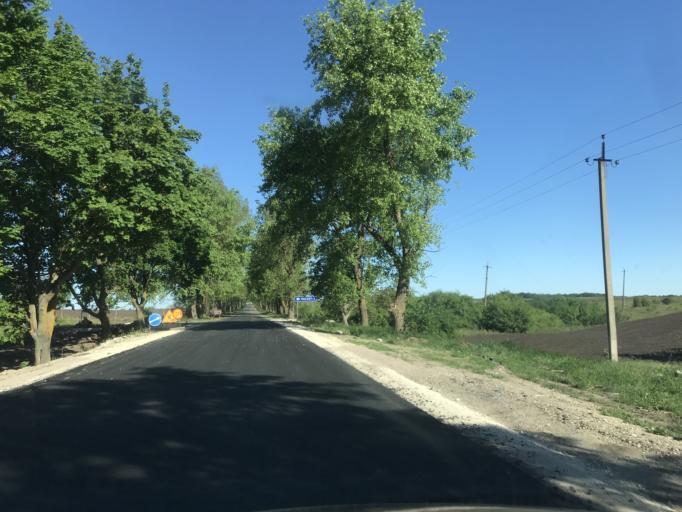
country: MD
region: Orhei
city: Orhei
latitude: 47.2562
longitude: 28.8028
